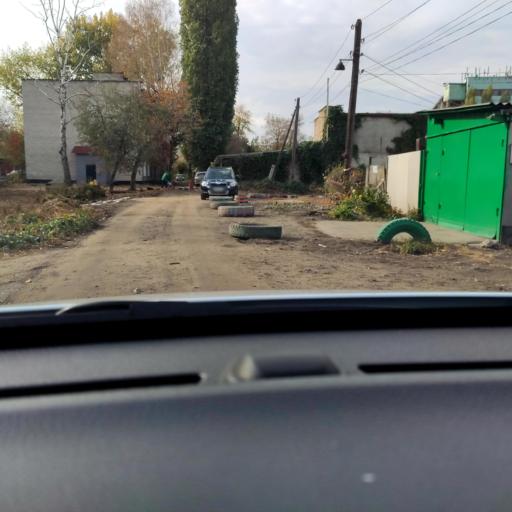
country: RU
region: Voronezj
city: Voronezh
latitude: 51.6744
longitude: 39.1765
